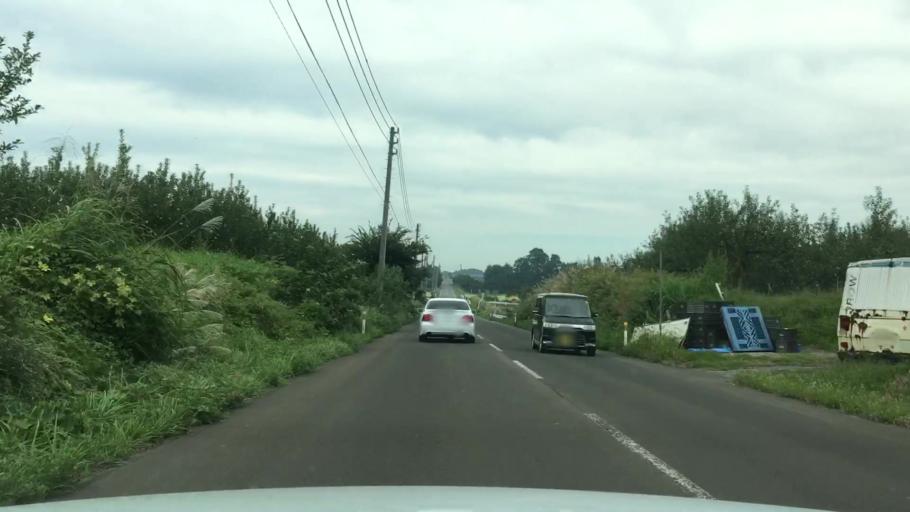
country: JP
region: Aomori
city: Hirosaki
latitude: 40.6485
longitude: 140.4230
